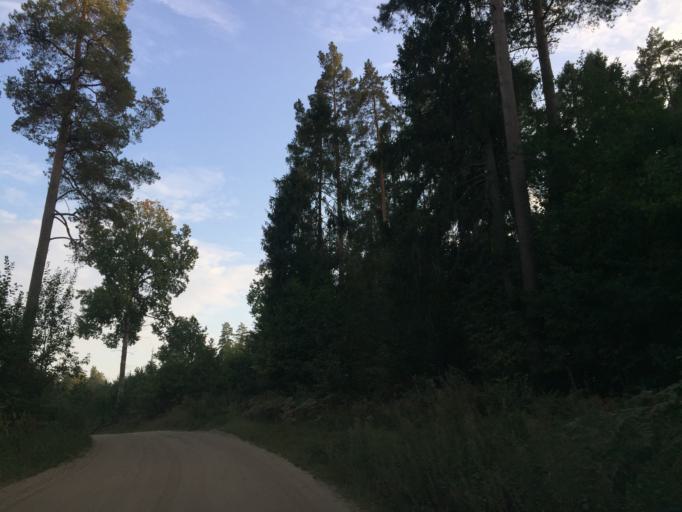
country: LV
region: Baldone
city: Baldone
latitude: 56.7650
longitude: 24.4074
